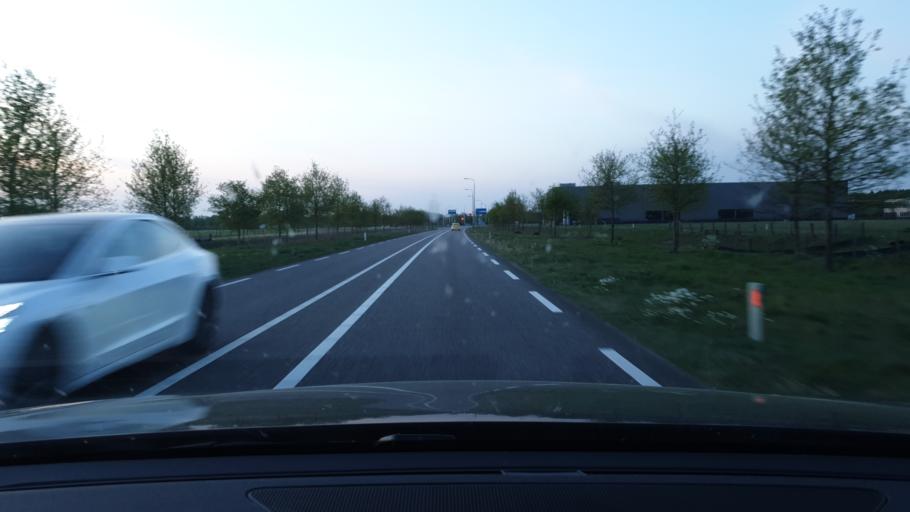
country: NL
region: North Brabant
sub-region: Gemeente Eersel
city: Eersel
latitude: 51.3597
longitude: 5.2713
